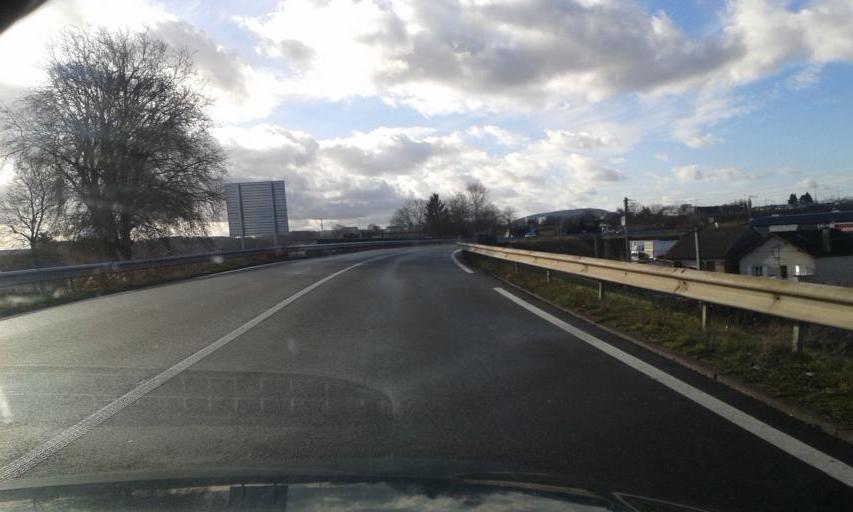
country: FR
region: Picardie
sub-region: Departement de l'Oise
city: Venette
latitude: 49.4091
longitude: 2.7953
